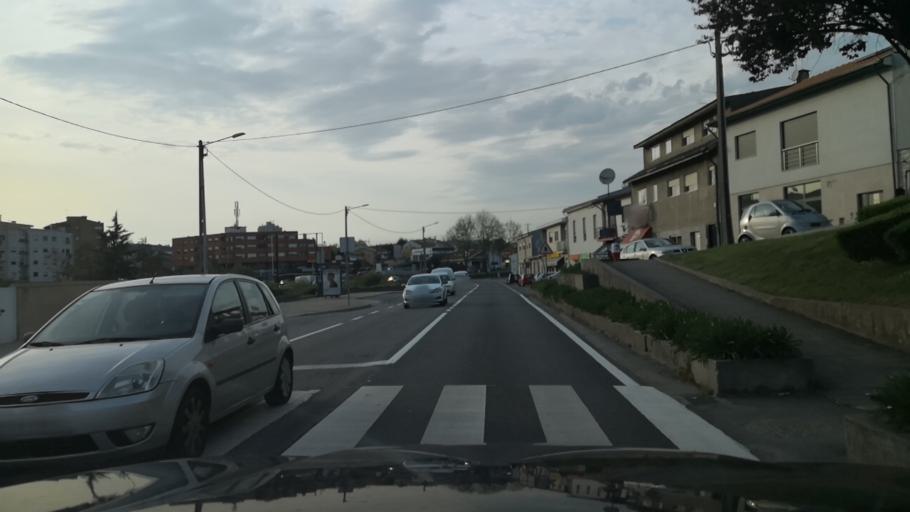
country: PT
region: Porto
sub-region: Valongo
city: Campo
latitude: 41.1867
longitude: -8.4881
